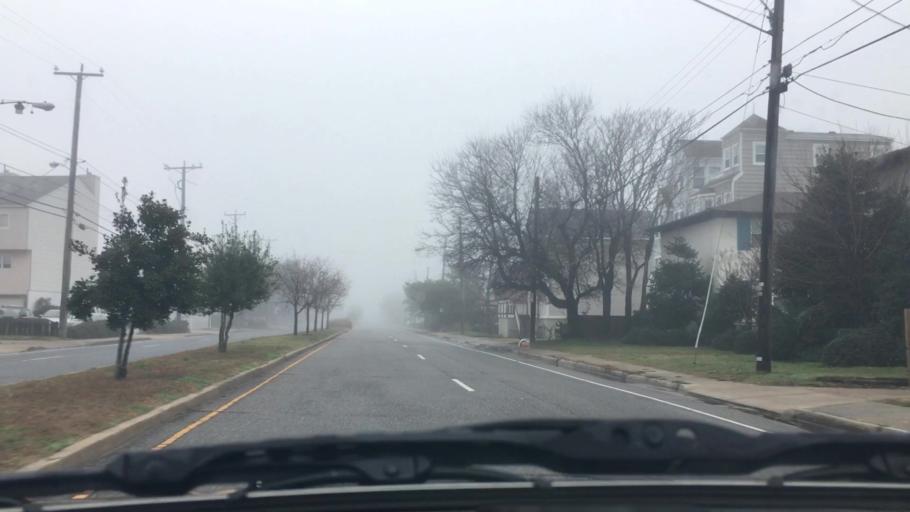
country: US
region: Virginia
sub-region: City of Hampton
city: East Hampton
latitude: 36.9657
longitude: -76.2738
